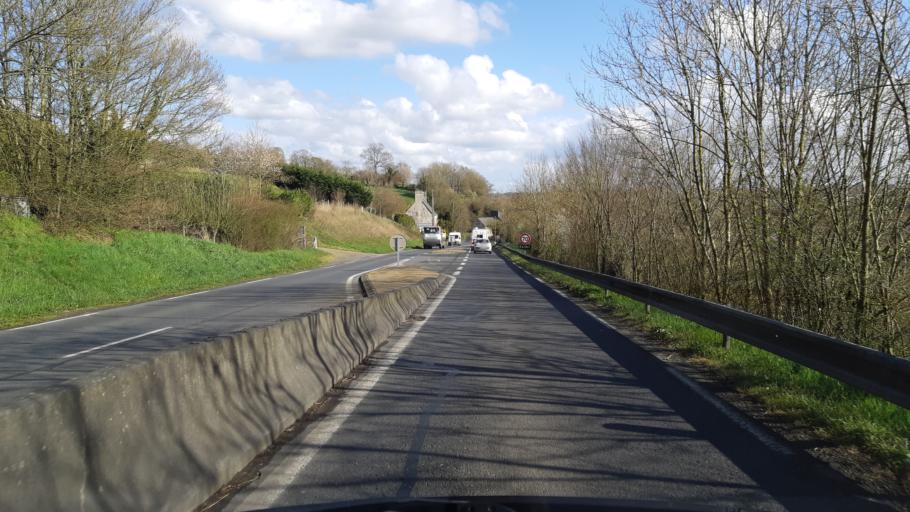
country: FR
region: Lower Normandy
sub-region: Departement de la Manche
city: Agneaux
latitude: 49.0946
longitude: -1.1206
